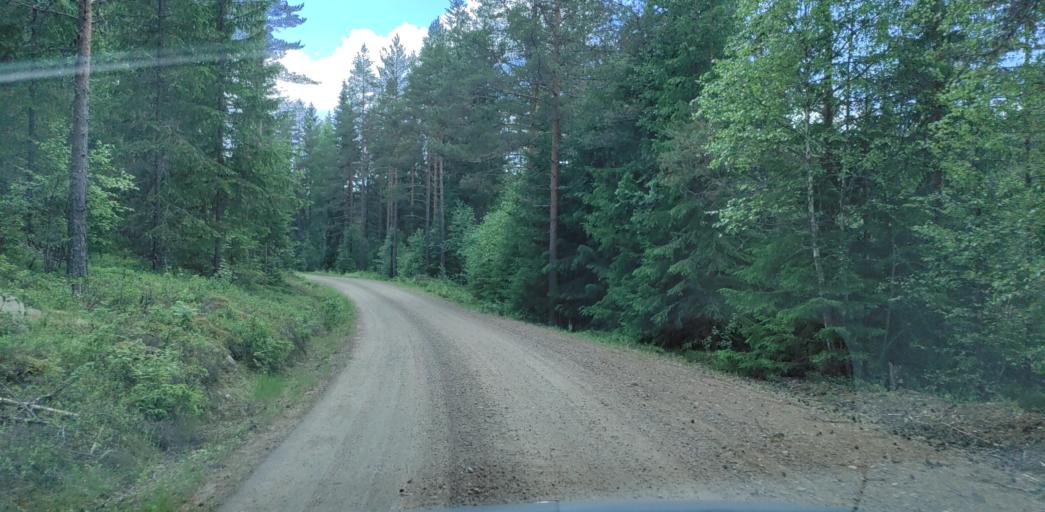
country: SE
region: Vaermland
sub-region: Hagfors Kommun
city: Ekshaerad
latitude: 60.0806
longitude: 13.2940
